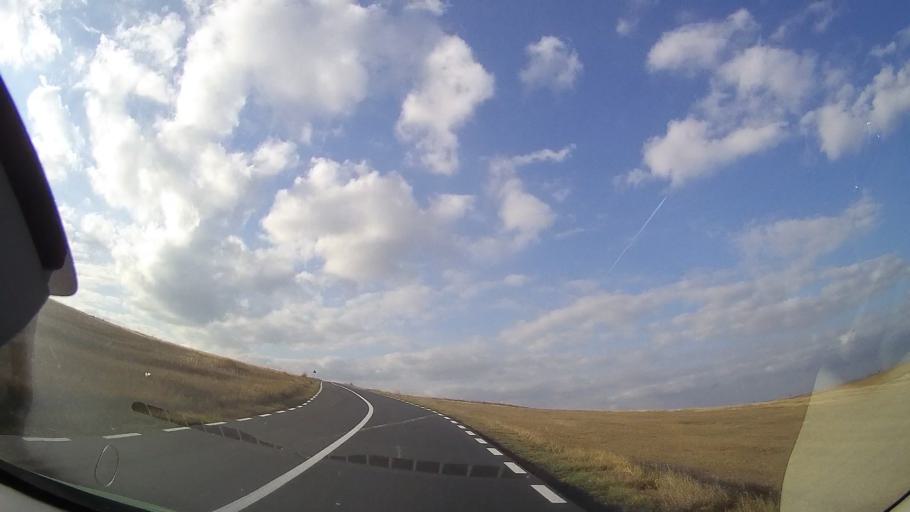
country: RO
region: Constanta
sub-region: Comuna Albesti
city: Albesti
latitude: 43.8082
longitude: 28.4181
